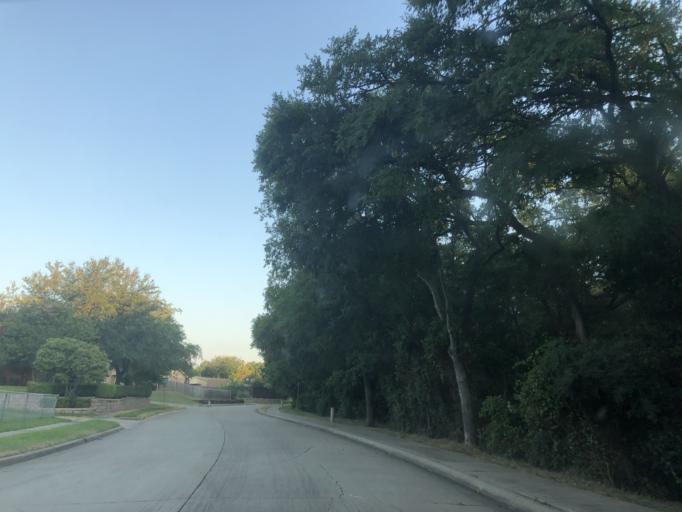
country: US
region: Texas
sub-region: Dallas County
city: Sunnyvale
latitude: 32.8411
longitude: -96.5736
